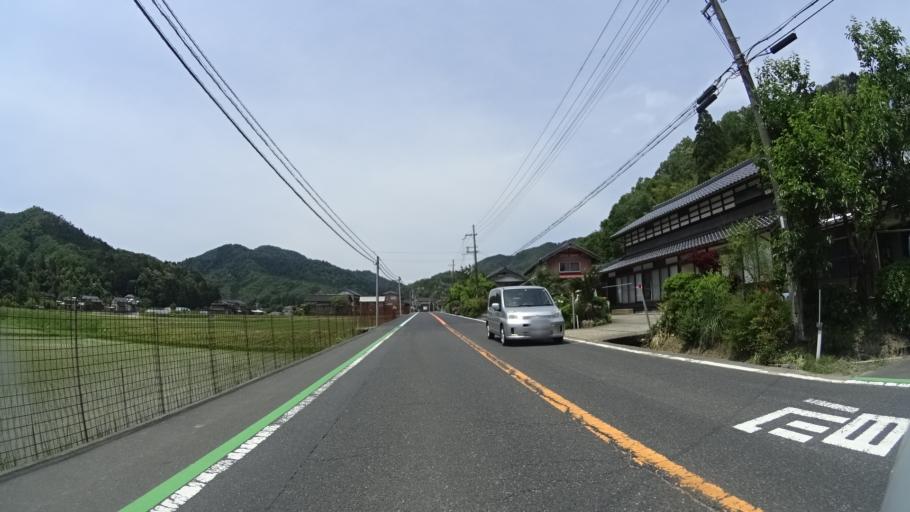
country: JP
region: Kyoto
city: Miyazu
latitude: 35.5802
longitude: 135.0257
